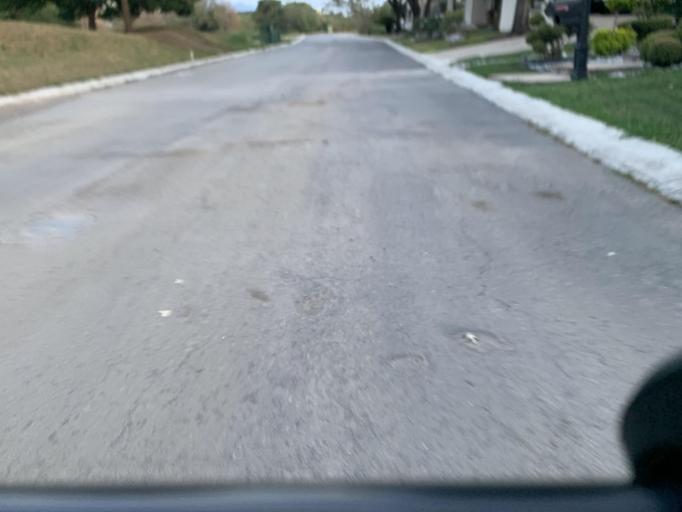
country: MX
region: Nuevo Leon
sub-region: Juarez
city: Bosques de San Pedro
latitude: 25.5206
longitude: -100.1954
